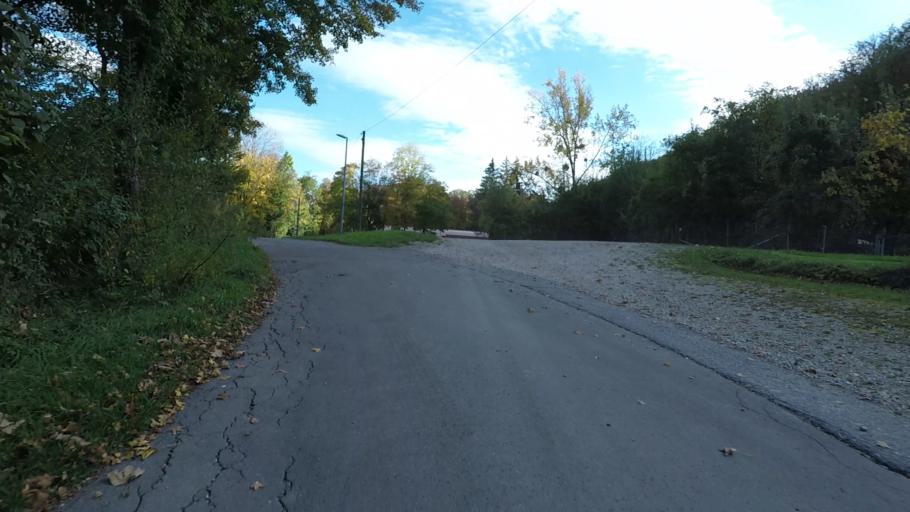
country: DE
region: Baden-Wuerttemberg
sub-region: Tuebingen Region
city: Pfullingen
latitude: 48.4497
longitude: 9.2274
